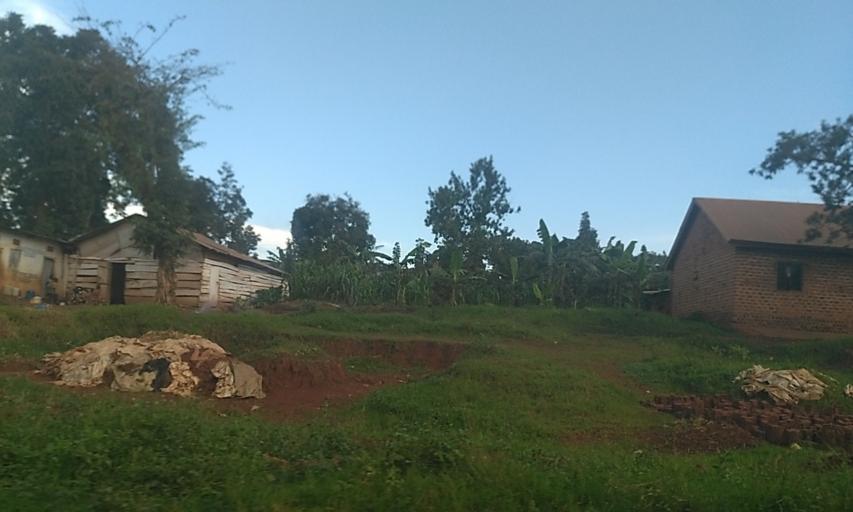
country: UG
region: Central Region
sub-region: Wakiso District
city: Kajansi
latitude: 0.2514
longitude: 32.5043
